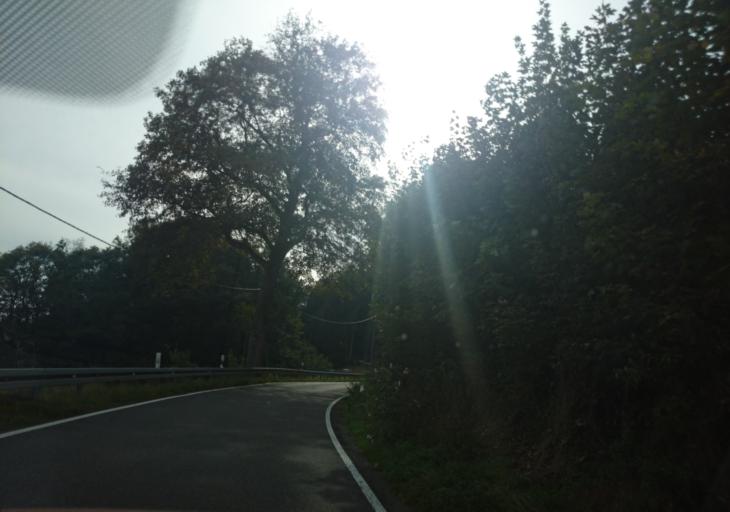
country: DE
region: Saxony
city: Zschopau
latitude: 50.7604
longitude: 13.0877
